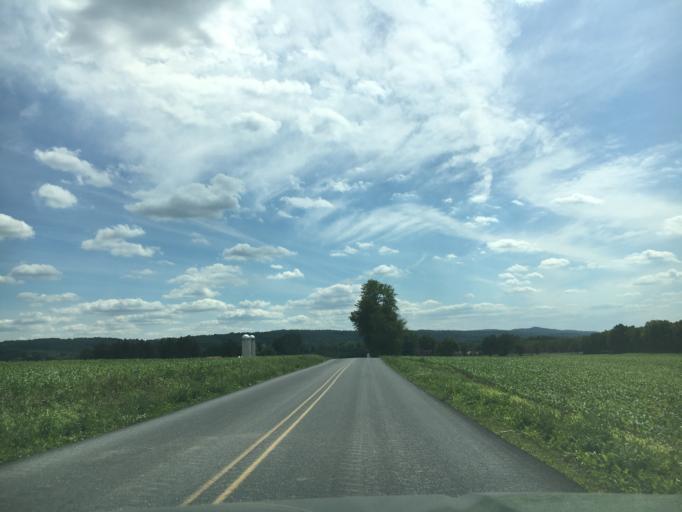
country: US
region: Pennsylvania
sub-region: Berks County
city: Fleetwood
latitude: 40.4673
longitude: -75.8094
